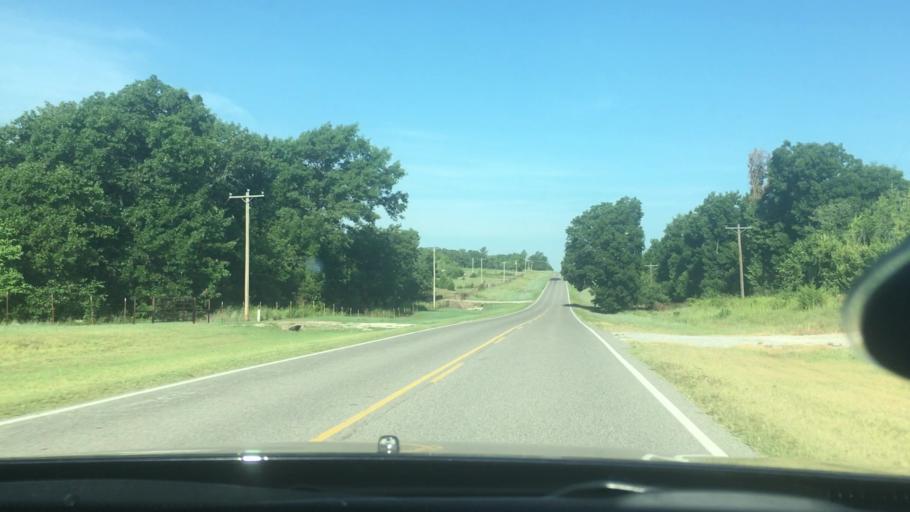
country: US
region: Oklahoma
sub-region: Garvin County
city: Wynnewood
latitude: 34.6518
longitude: -97.2585
